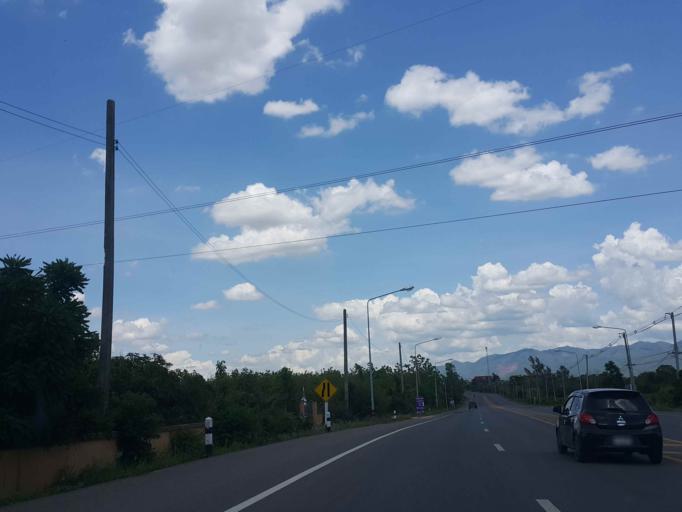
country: TH
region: Phrae
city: Nong Muang Khai
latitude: 18.2039
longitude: 100.2120
